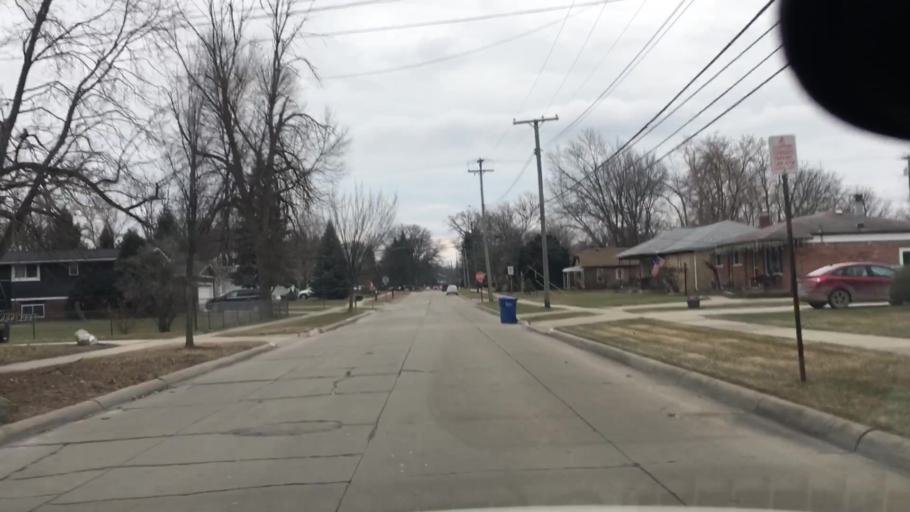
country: US
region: Michigan
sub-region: Oakland County
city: Madison Heights
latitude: 42.5027
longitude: -83.0738
